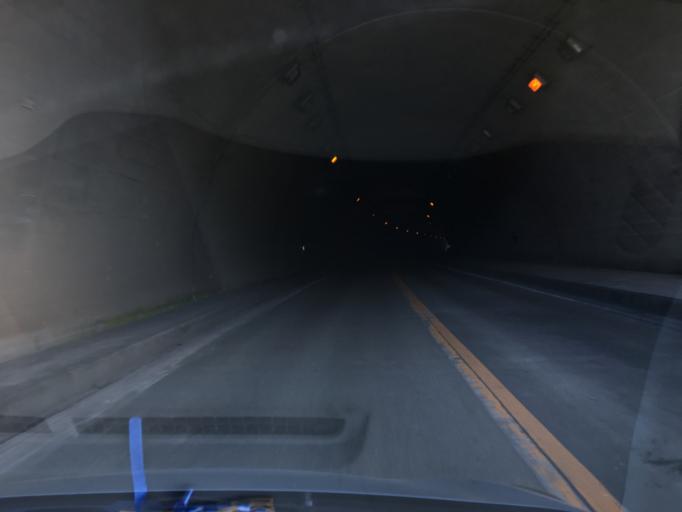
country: JP
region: Hyogo
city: Toyooka
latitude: 35.4518
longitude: 134.7702
